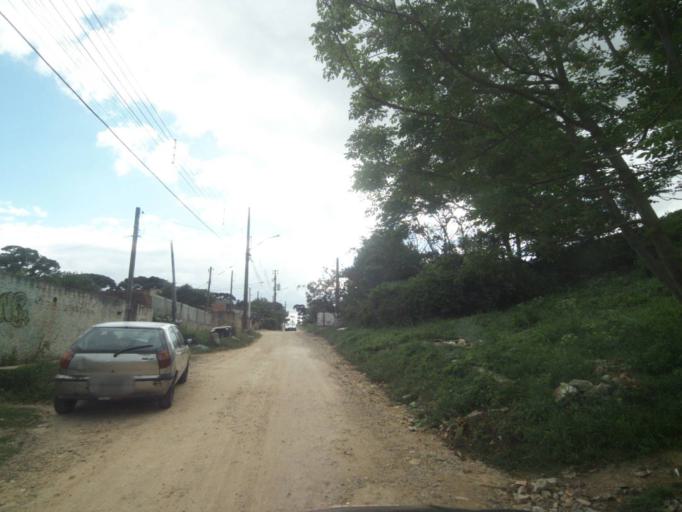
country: BR
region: Parana
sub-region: Sao Jose Dos Pinhais
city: Sao Jose dos Pinhais
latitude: -25.5474
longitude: -49.2469
